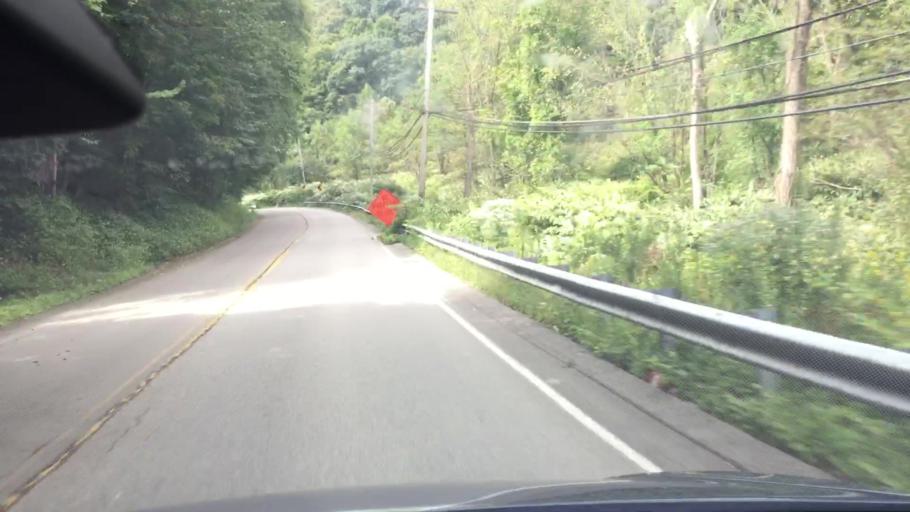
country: US
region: Pennsylvania
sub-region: Allegheny County
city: Monroeville
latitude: 40.4279
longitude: -79.7665
